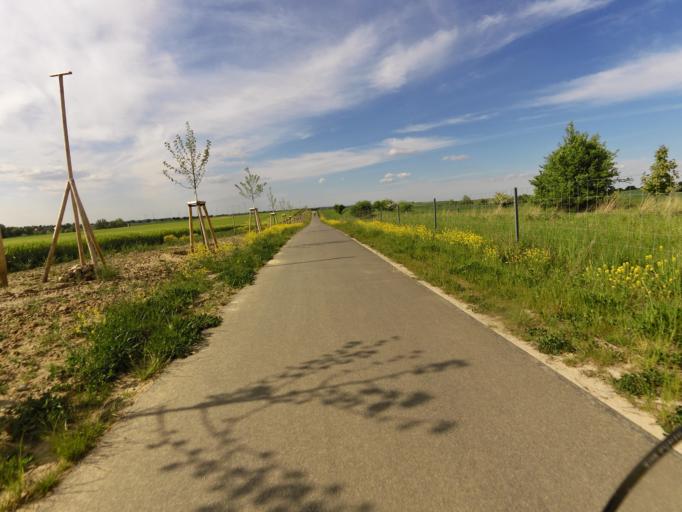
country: DE
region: Brandenburg
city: Mescherin
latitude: 53.2765
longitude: 14.4210
